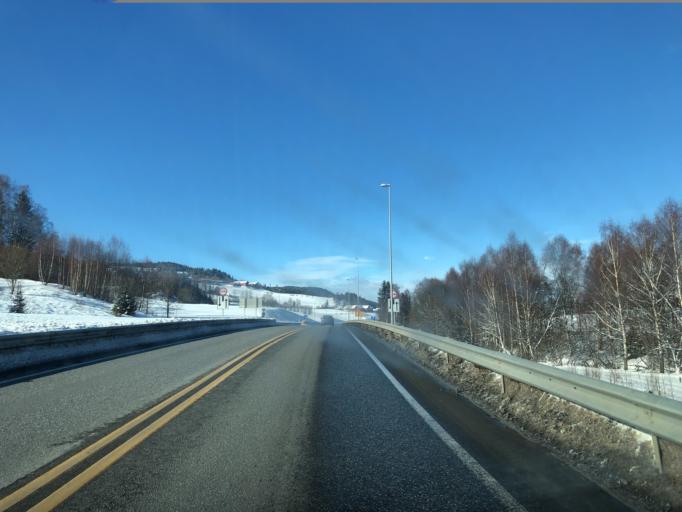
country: NO
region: Oppland
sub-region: Lunner
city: Roa
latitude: 60.3227
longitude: 10.5809
